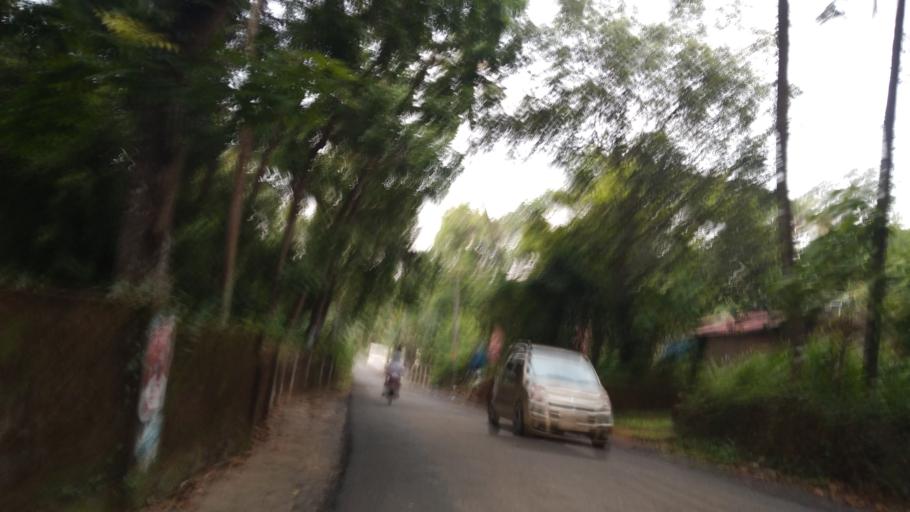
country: IN
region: Kerala
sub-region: Ernakulam
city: Perumbavoor
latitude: 10.0697
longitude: 76.5045
